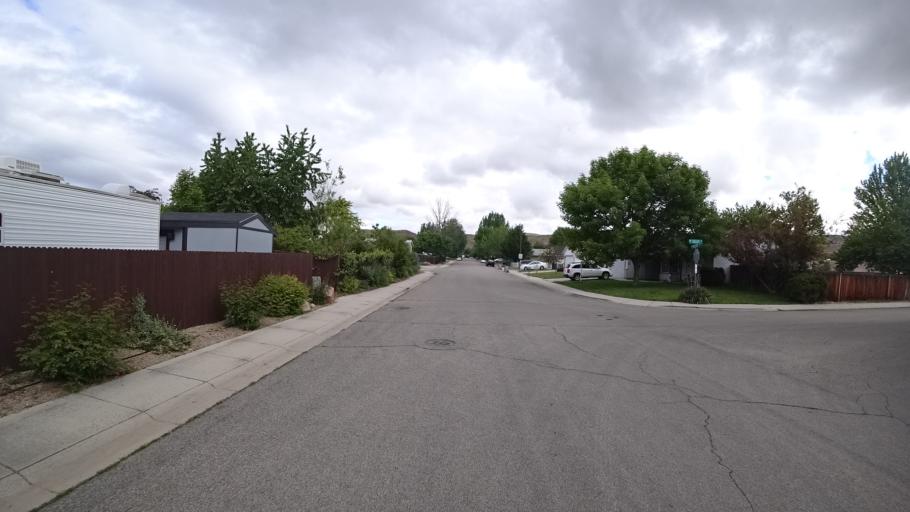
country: US
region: Idaho
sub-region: Ada County
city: Eagle
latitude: 43.6780
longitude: -116.2847
